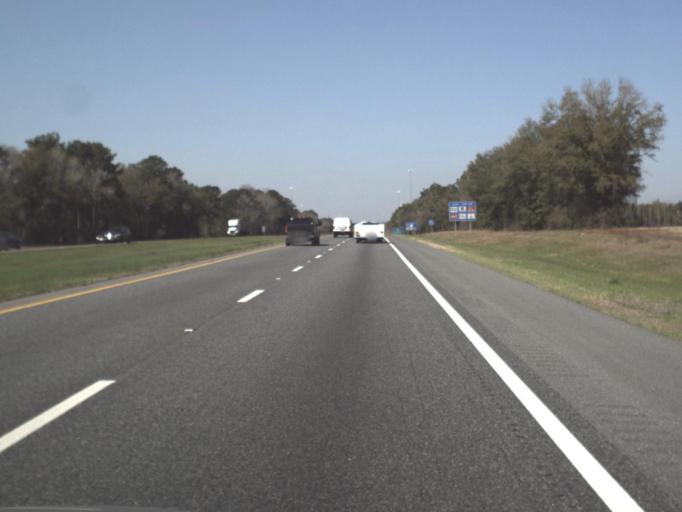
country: US
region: Florida
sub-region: Jackson County
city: Marianna
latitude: 30.7185
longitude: -85.1710
